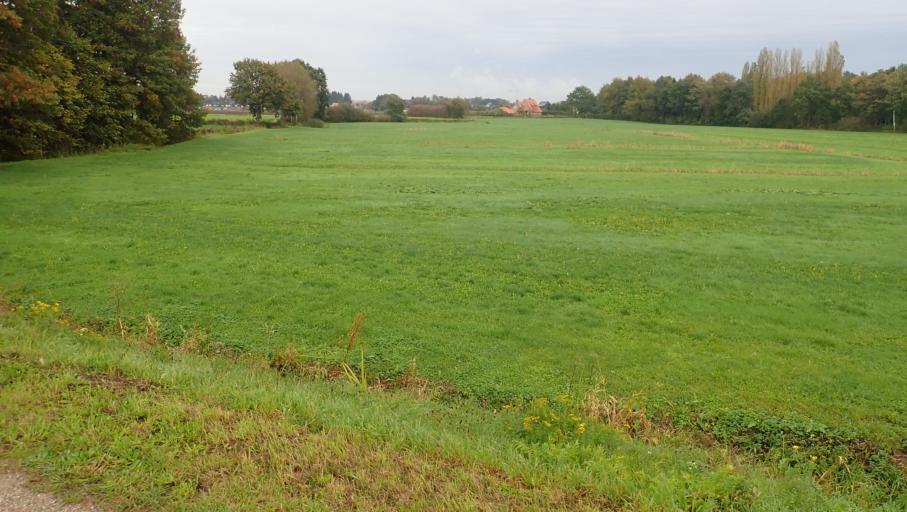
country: BE
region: Flanders
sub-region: Provincie Antwerpen
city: Berlaar
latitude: 51.1346
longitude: 4.6678
